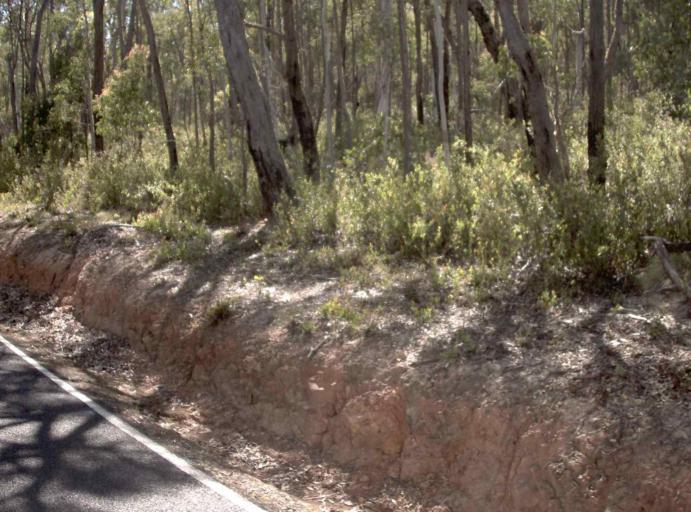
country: AU
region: New South Wales
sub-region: Bombala
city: Bombala
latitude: -37.1407
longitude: 148.7293
